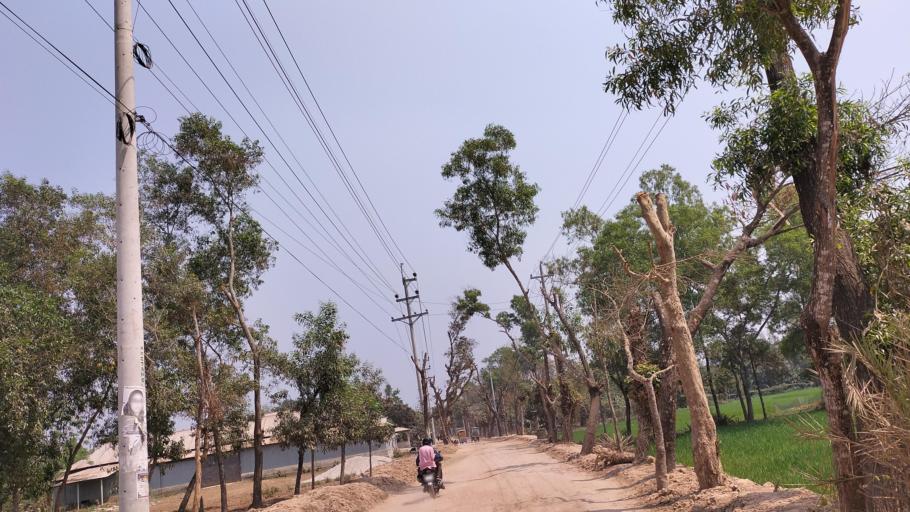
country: BD
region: Dhaka
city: Sakhipur
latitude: 24.3073
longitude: 90.3101
